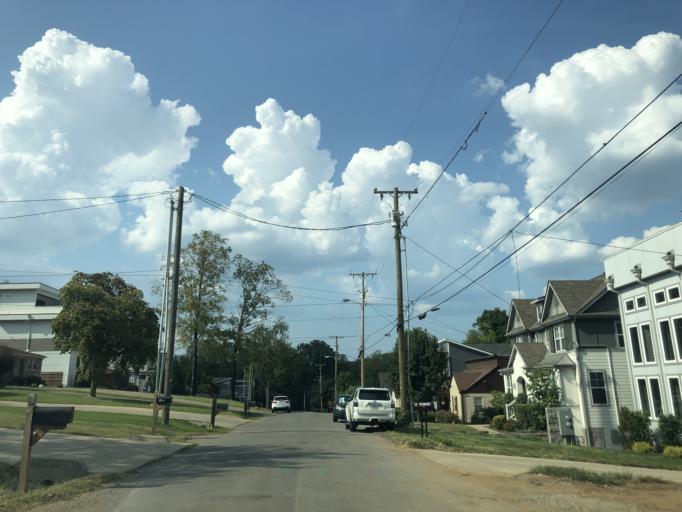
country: US
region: Tennessee
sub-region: Davidson County
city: Oak Hill
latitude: 36.1210
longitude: -86.7808
